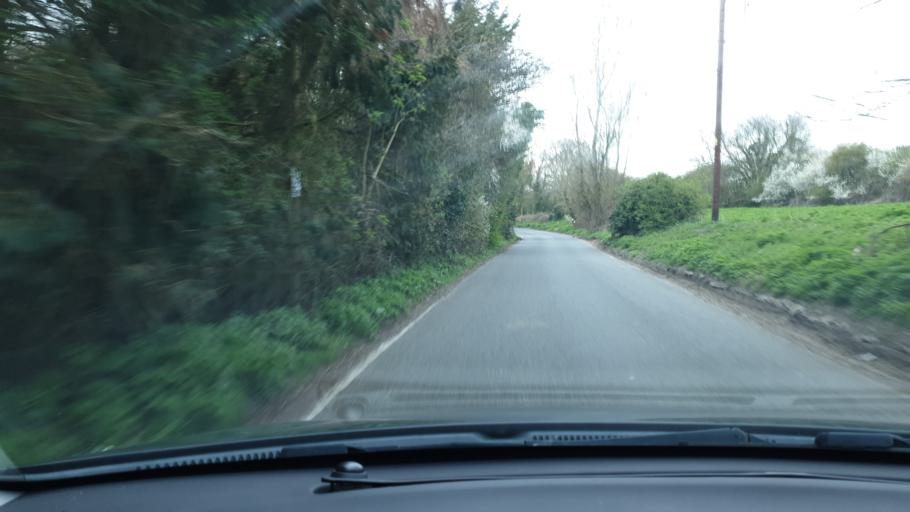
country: GB
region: England
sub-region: Essex
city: Mistley
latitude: 51.9210
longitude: 1.1342
